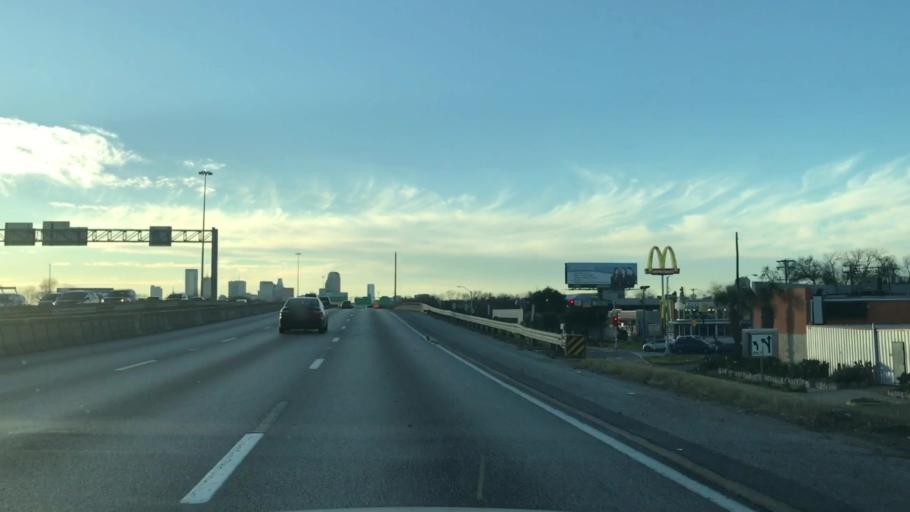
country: US
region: Texas
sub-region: Dallas County
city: Dallas
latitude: 32.7914
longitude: -96.7485
